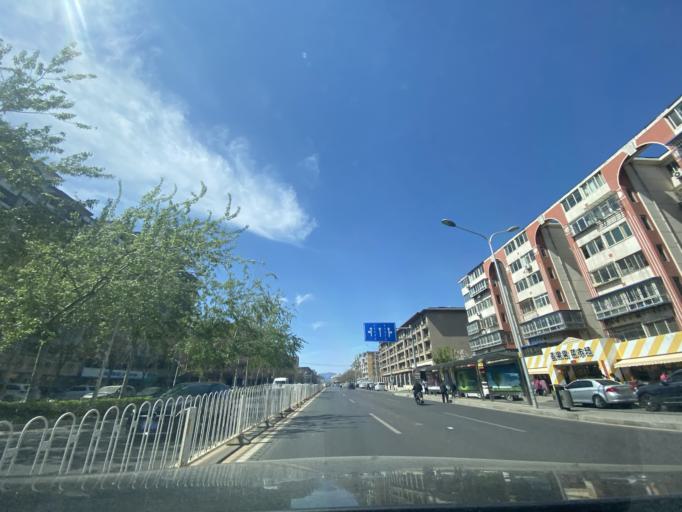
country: CN
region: Beijing
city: Sijiqing
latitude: 39.9280
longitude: 116.2559
